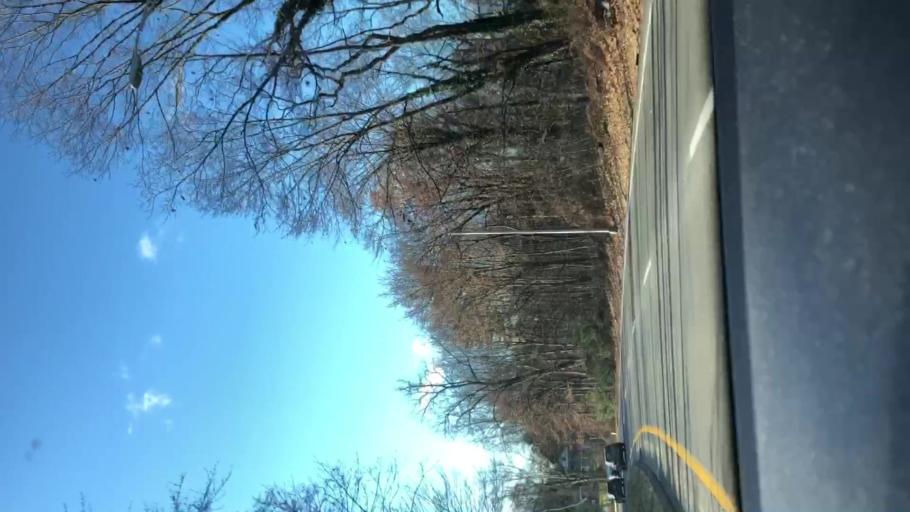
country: US
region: New York
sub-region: Westchester County
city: Tuckahoe
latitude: 40.9363
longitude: -73.8082
